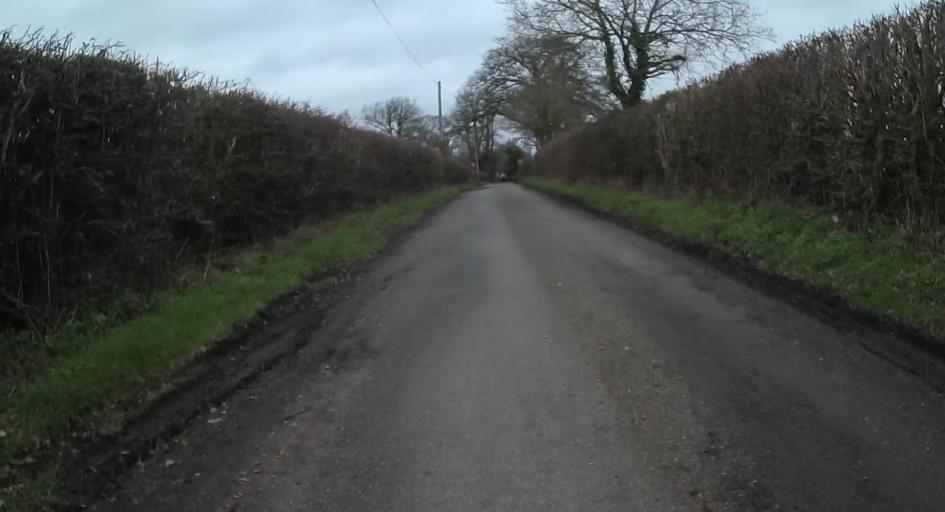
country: GB
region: England
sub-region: West Berkshire
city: Stratfield Mortimer
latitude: 51.3716
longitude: -1.0464
